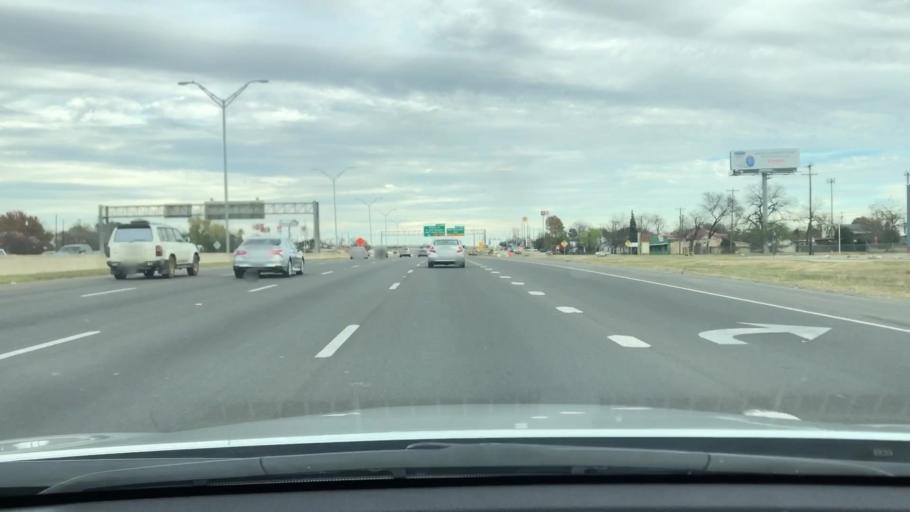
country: US
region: Texas
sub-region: Bexar County
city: San Antonio
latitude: 29.4380
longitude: -98.4650
